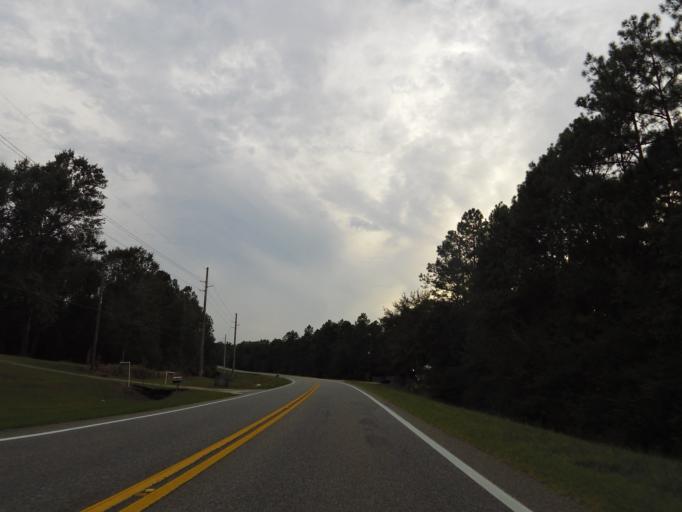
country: US
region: Alabama
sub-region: Baldwin County
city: Bay Minette
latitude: 30.9660
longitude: -87.6505
